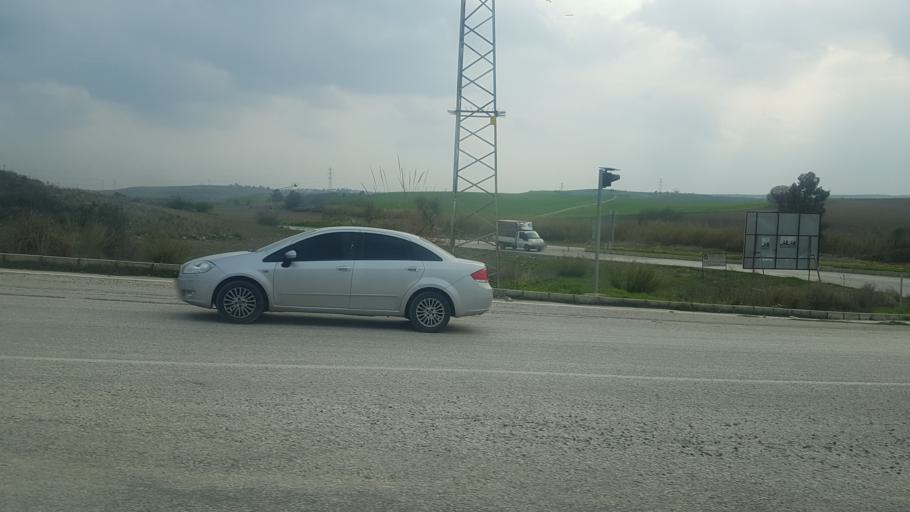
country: TR
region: Mersin
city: Yenice
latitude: 37.0555
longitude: 35.1688
